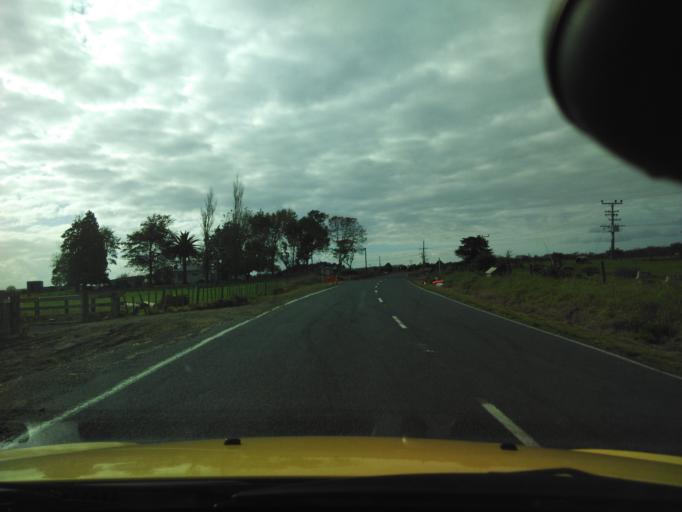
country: NZ
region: Waikato
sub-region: Waikato District
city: Te Kauwhata
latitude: -37.4775
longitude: 175.1437
